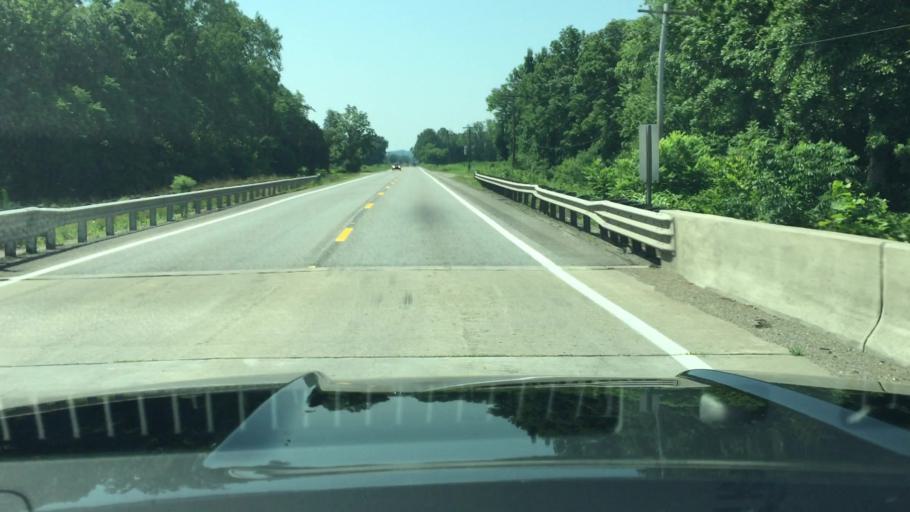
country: US
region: West Virginia
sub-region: Putnam County
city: Buffalo
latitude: 38.6902
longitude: -81.9652
